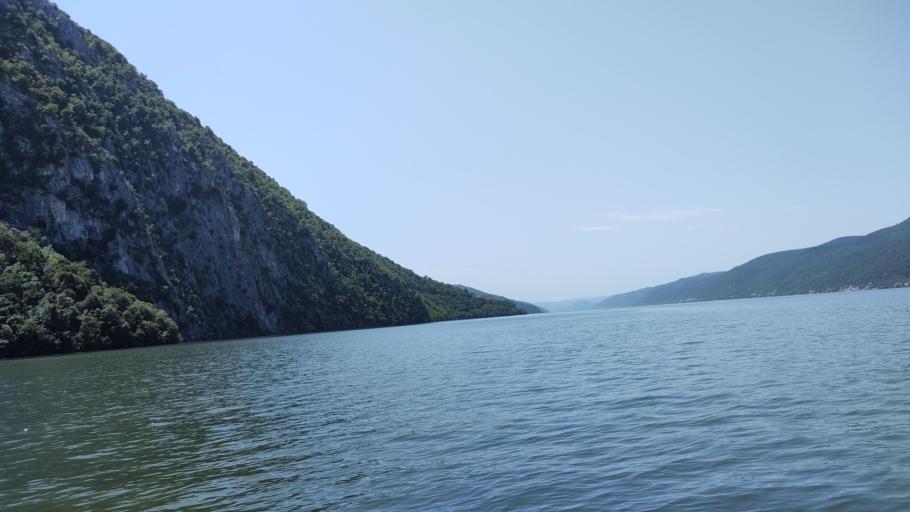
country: RO
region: Mehedinti
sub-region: Comuna Dubova
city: Dubova
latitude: 44.5861
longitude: 22.2539
